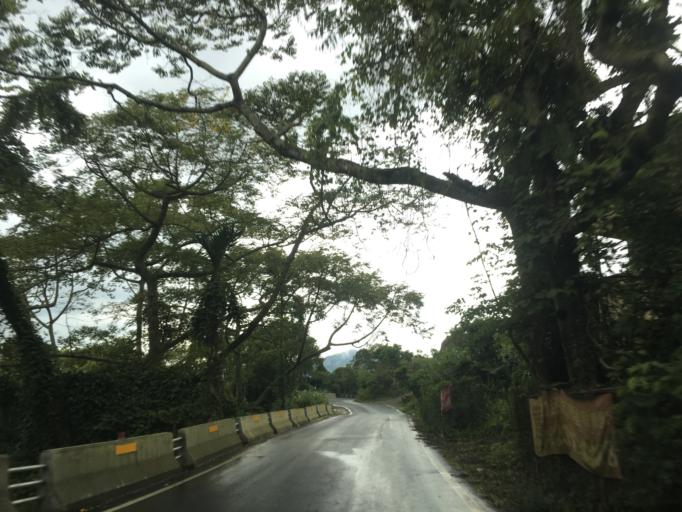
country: TW
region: Taiwan
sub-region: Chiayi
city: Jiayi Shi
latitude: 23.4458
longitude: 120.6668
